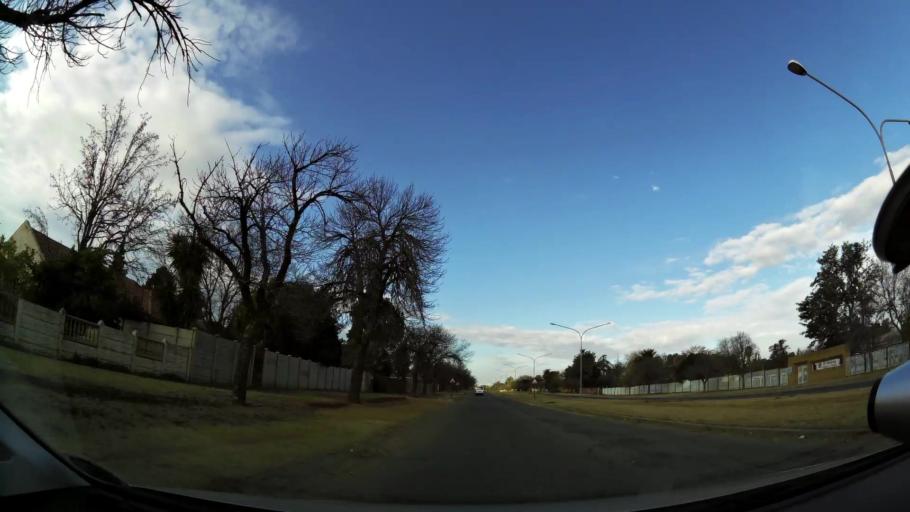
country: ZA
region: Orange Free State
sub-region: Lejweleputswa District Municipality
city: Welkom
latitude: -27.9891
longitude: 26.7172
